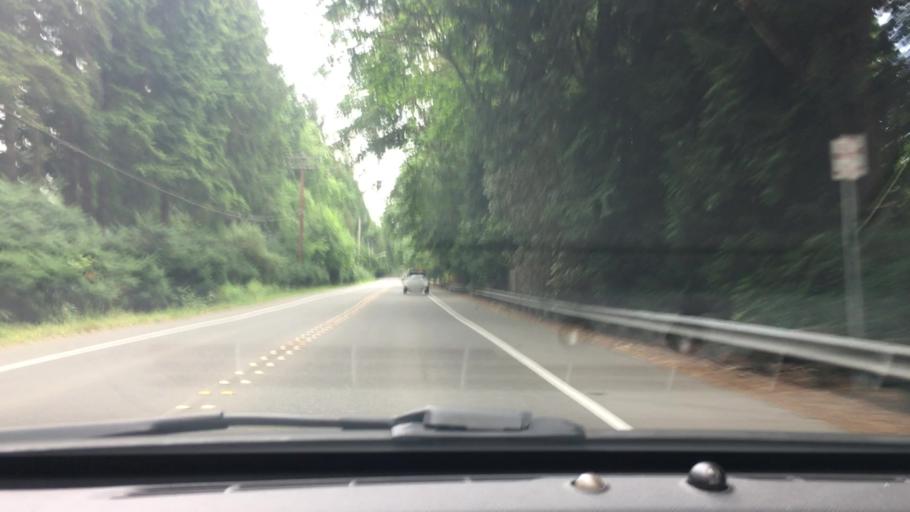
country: US
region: Washington
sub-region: King County
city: West Lake Sammamish
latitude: 47.5598
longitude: -122.0870
